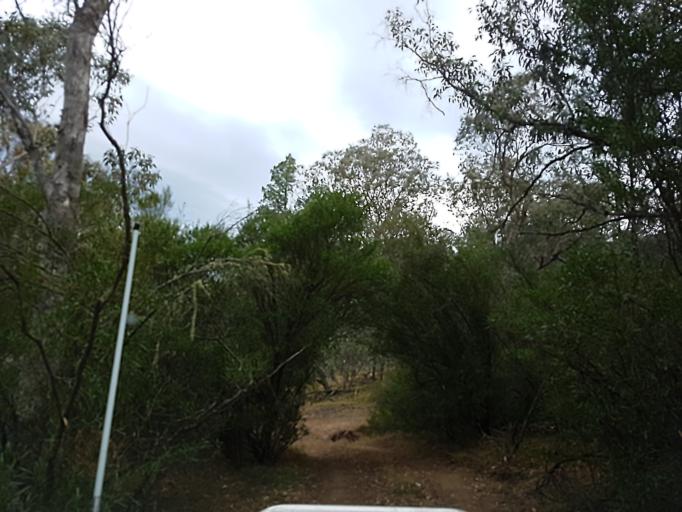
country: AU
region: New South Wales
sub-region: Snowy River
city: Jindabyne
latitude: -36.9595
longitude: 148.4108
